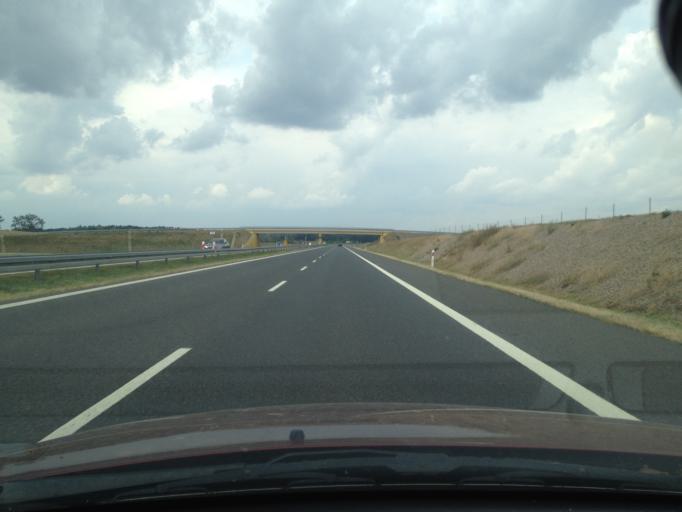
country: PL
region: West Pomeranian Voivodeship
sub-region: Powiat mysliborski
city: Mysliborz
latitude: 52.9845
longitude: 14.8834
